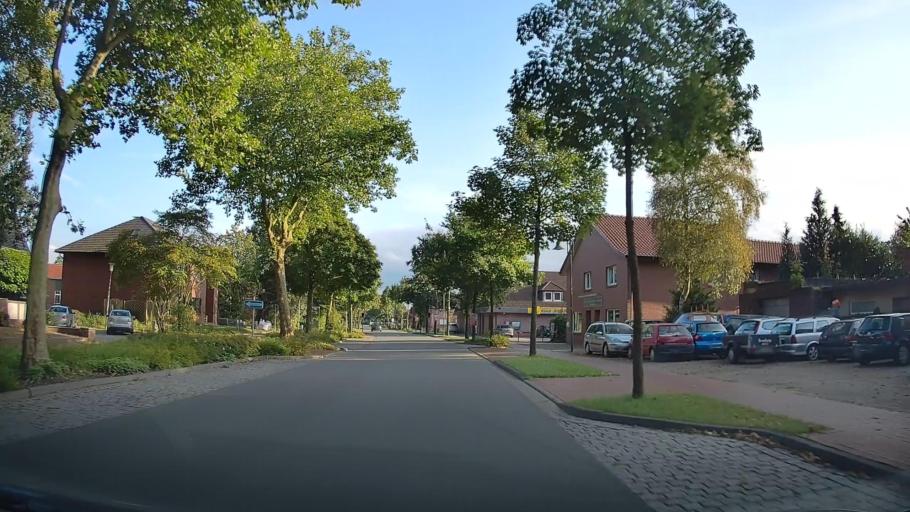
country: DE
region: Lower Saxony
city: Hilkenbrook
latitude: 53.0439
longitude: 7.7376
